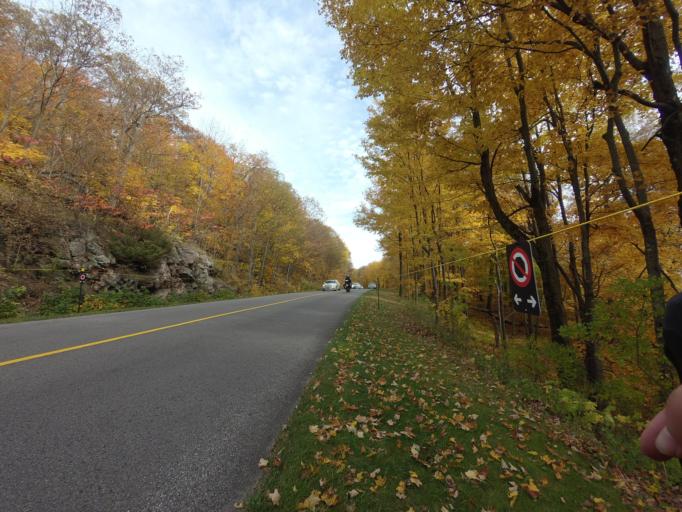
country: CA
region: Quebec
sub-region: Outaouais
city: Gatineau
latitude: 45.4925
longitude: -75.8616
